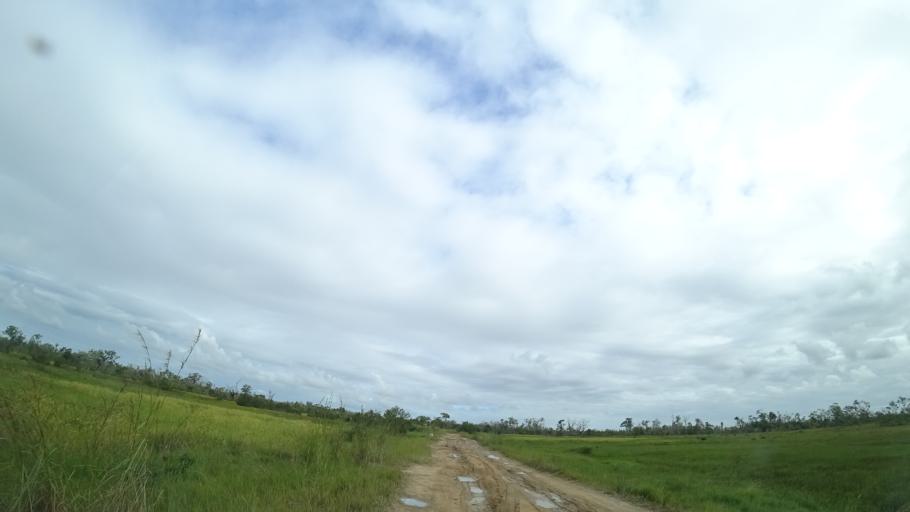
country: MZ
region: Sofala
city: Dondo
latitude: -19.5893
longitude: 35.0855
